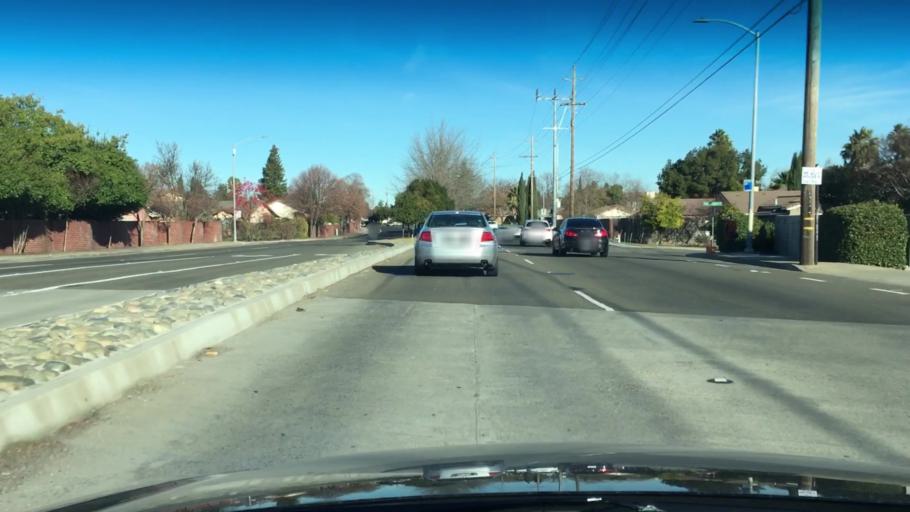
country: US
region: California
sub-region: Sacramento County
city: Parkway
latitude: 38.4633
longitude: -121.4466
